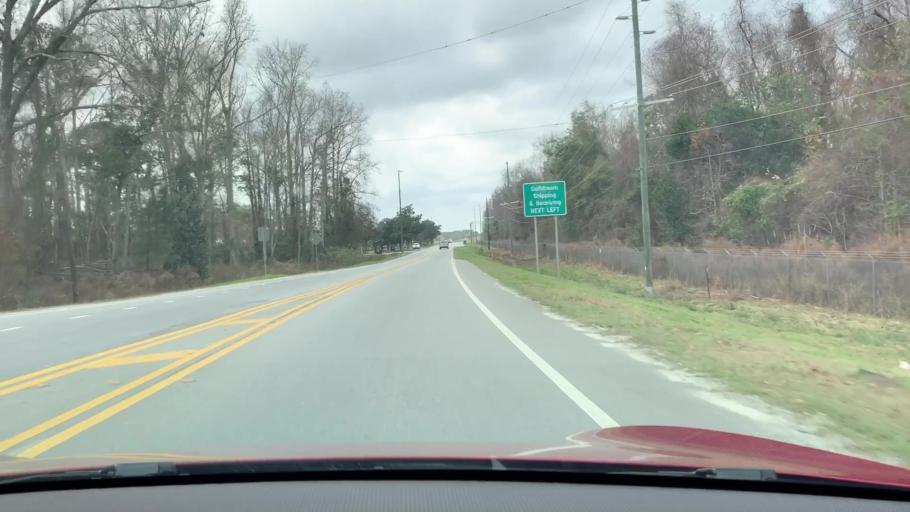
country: US
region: Georgia
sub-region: Chatham County
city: Port Wentworth
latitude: 32.1417
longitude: -81.1934
